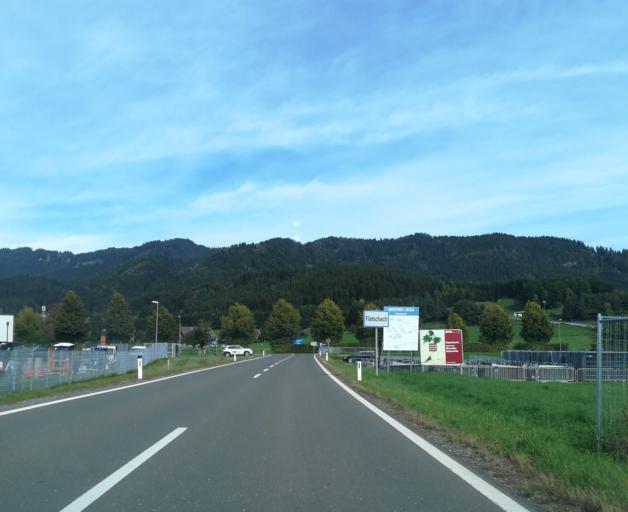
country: AT
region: Styria
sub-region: Politischer Bezirk Murtal
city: Flatschach
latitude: 47.2147
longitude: 14.7555
